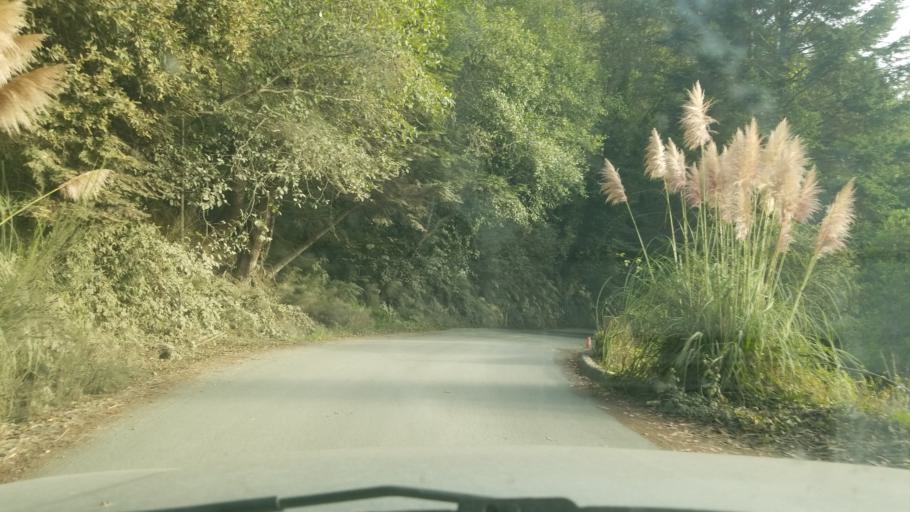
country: US
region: California
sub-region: Mendocino County
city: Fort Bragg
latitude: 39.4282
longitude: -123.7957
